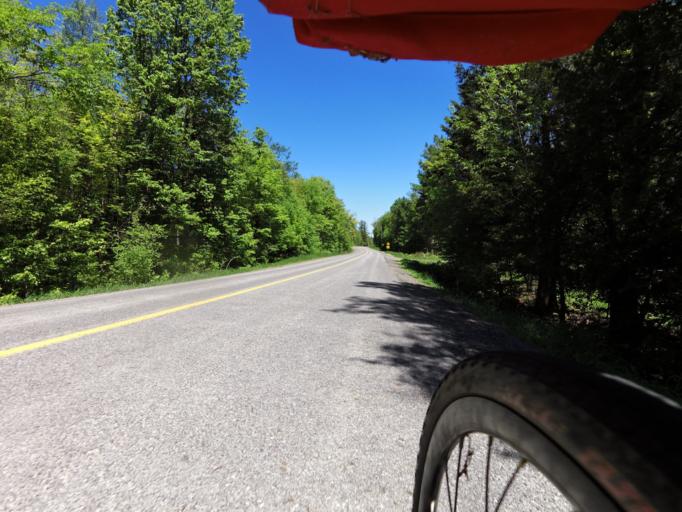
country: CA
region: Ontario
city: Carleton Place
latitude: 45.1669
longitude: -76.4213
